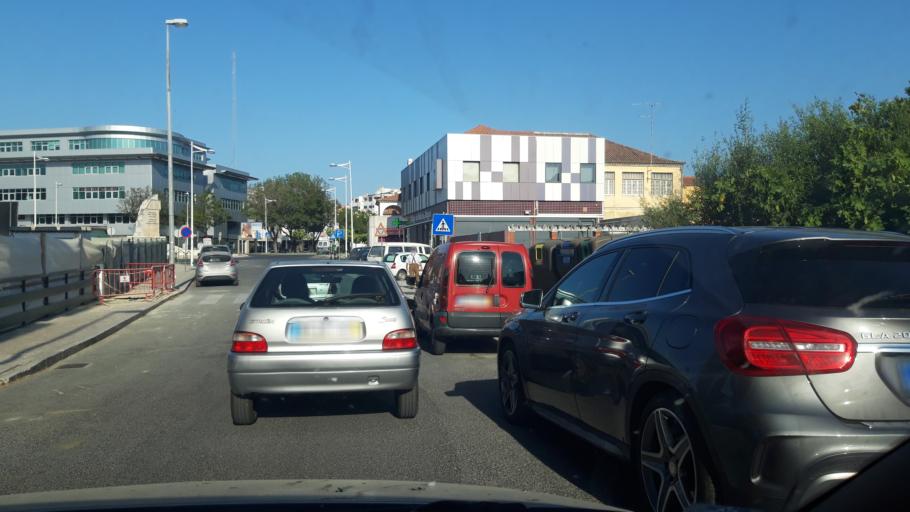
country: PT
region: Santarem
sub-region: Torres Novas
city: Torres Novas
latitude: 39.4776
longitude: -8.5383
